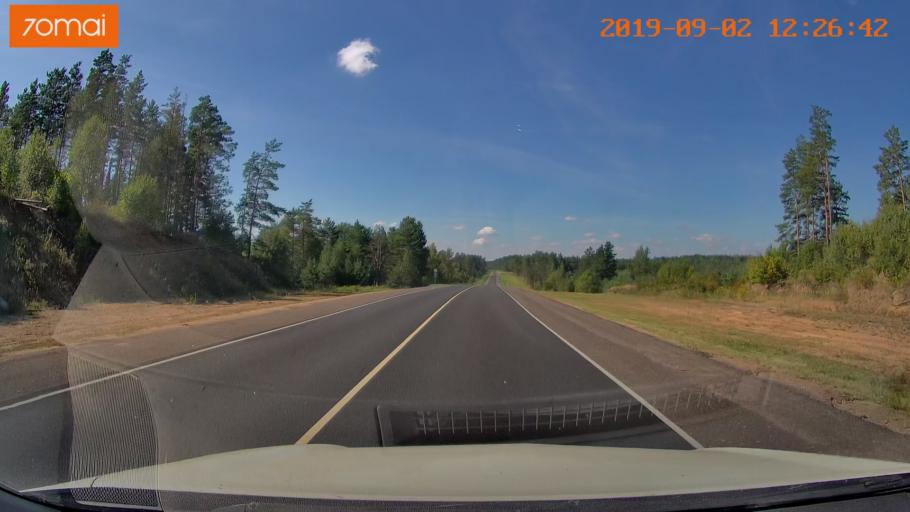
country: RU
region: Smolensk
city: Shumyachi
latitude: 53.8557
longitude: 32.5614
